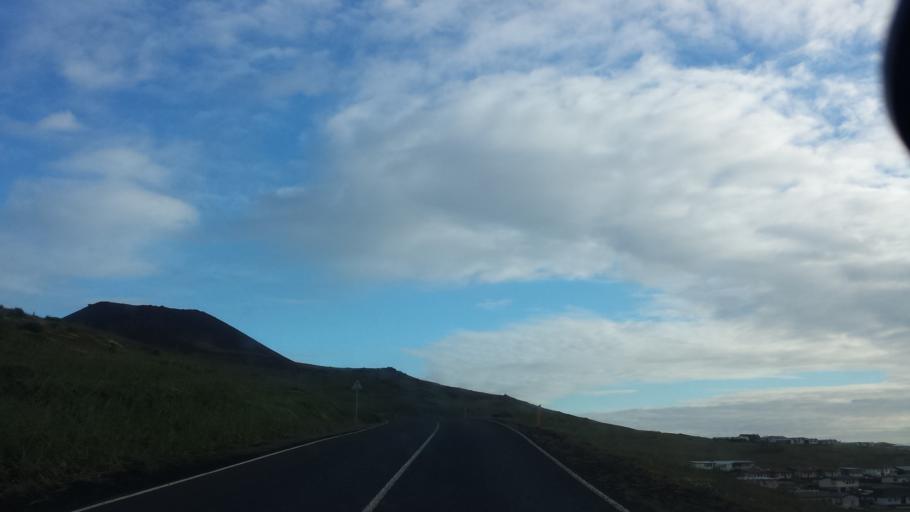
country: IS
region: South
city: Vestmannaeyjar
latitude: 63.4372
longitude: -20.2567
